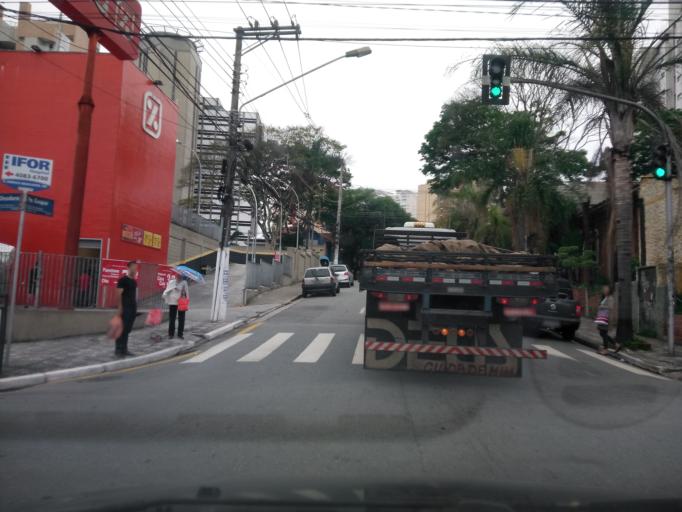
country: BR
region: Sao Paulo
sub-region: Sao Bernardo Do Campo
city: Sao Bernardo do Campo
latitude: -23.7174
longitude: -46.5491
